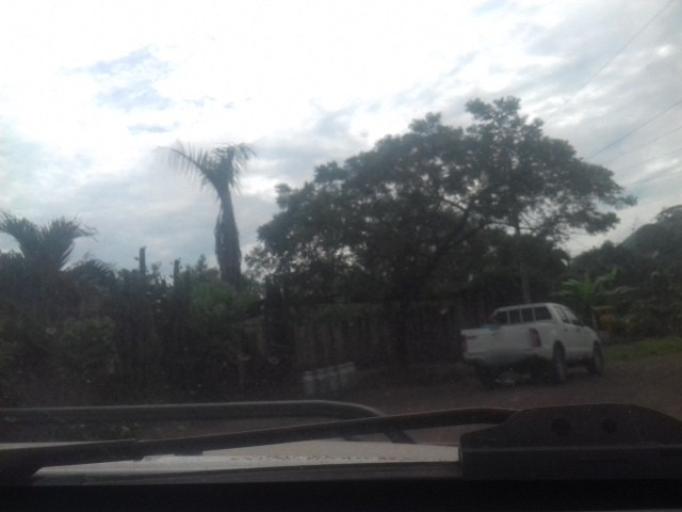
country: NI
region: Atlantico Norte (RAAN)
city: Waslala
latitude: 13.3899
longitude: -85.3288
